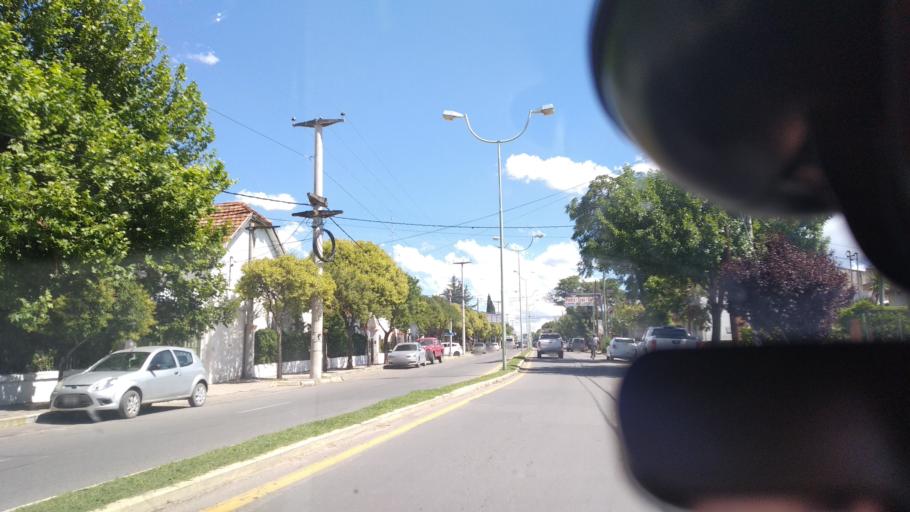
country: AR
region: Cordoba
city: Mina Clavero
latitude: -31.7219
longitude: -65.0068
